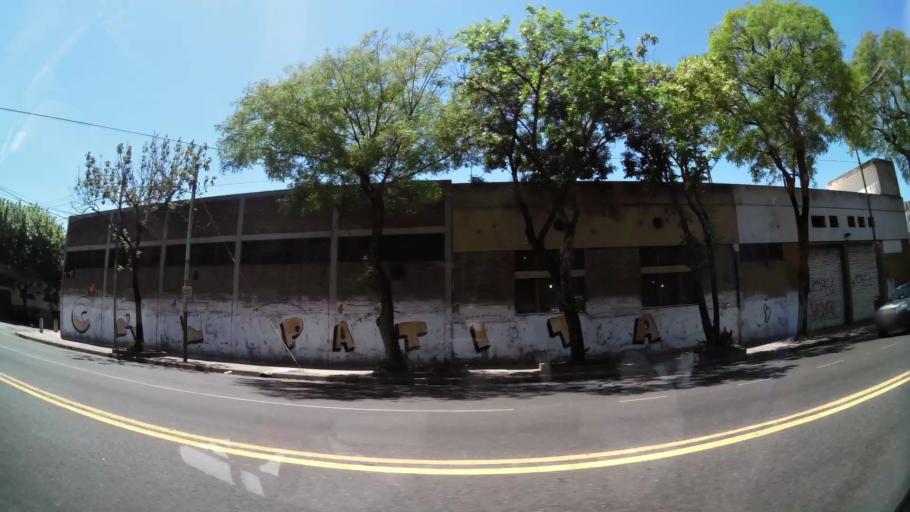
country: AR
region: Buenos Aires
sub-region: Partido de Avellaneda
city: Avellaneda
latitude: -34.6445
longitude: -58.3895
